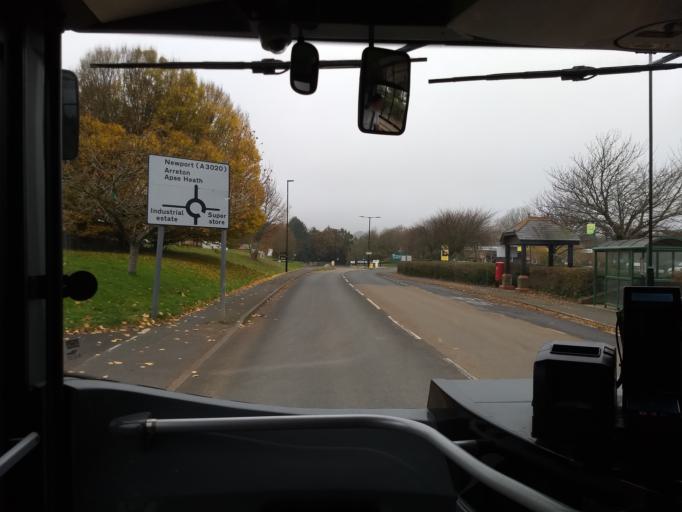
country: GB
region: England
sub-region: Isle of Wight
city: Shanklin
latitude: 50.6460
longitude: -1.1810
